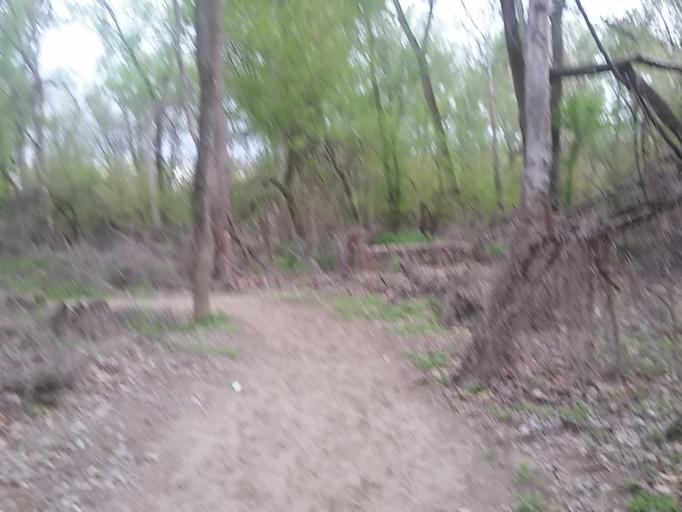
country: US
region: Nebraska
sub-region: Sarpy County
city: Bellevue
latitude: 41.1824
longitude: -95.8925
